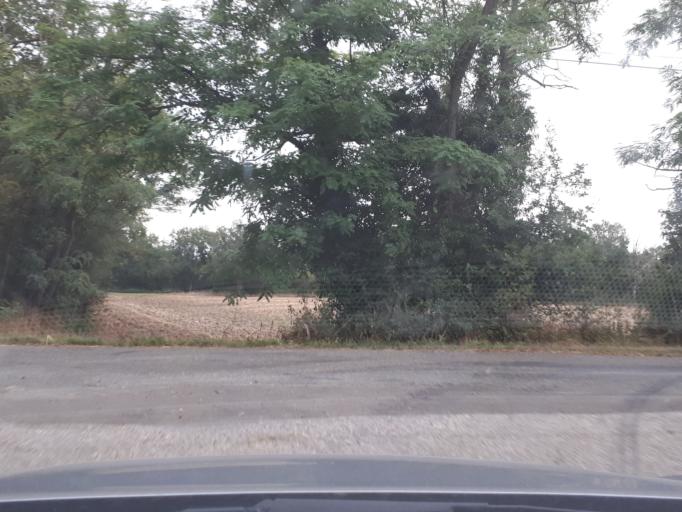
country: FR
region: Rhone-Alpes
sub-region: Departement de la Loire
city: Feurs
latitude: 45.7154
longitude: 4.2457
